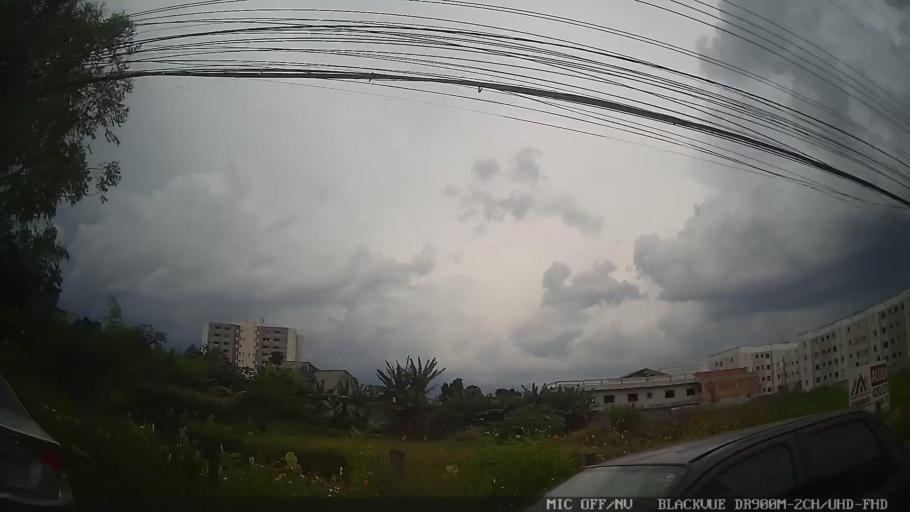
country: BR
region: Sao Paulo
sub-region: Suzano
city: Suzano
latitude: -23.5453
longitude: -46.2899
